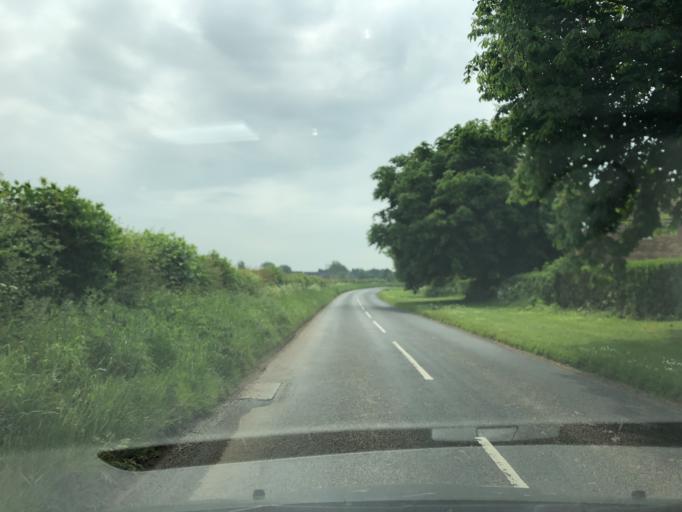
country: GB
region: England
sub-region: North Yorkshire
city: Boroughbridge
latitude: 54.1361
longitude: -1.4076
